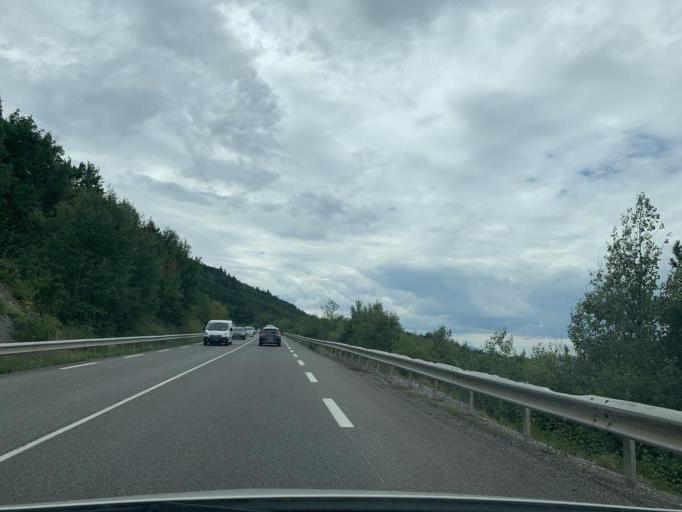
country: FR
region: Provence-Alpes-Cote d'Azur
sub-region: Departement des Hautes-Alpes
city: Embrun
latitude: 44.5280
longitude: 6.4224
